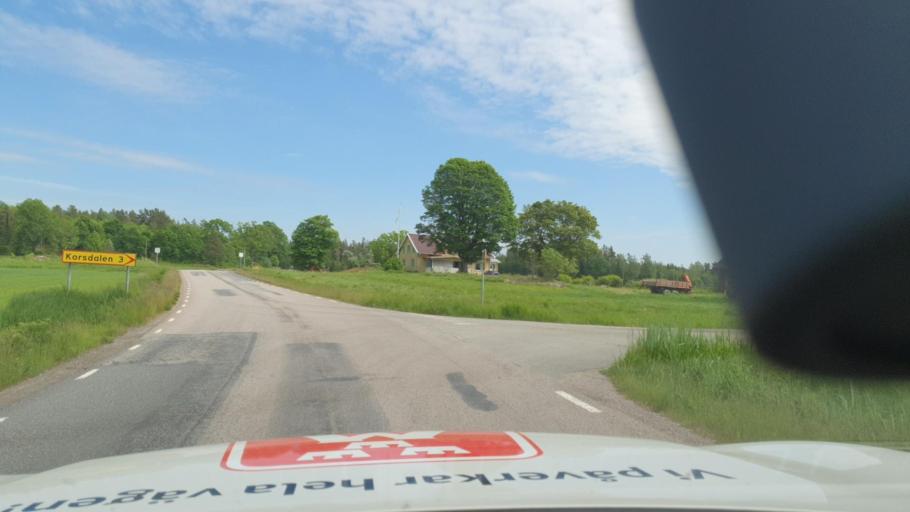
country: SE
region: Vaestra Goetaland
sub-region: Alingsas Kommun
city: Sollebrunn
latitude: 58.2130
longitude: 12.5307
